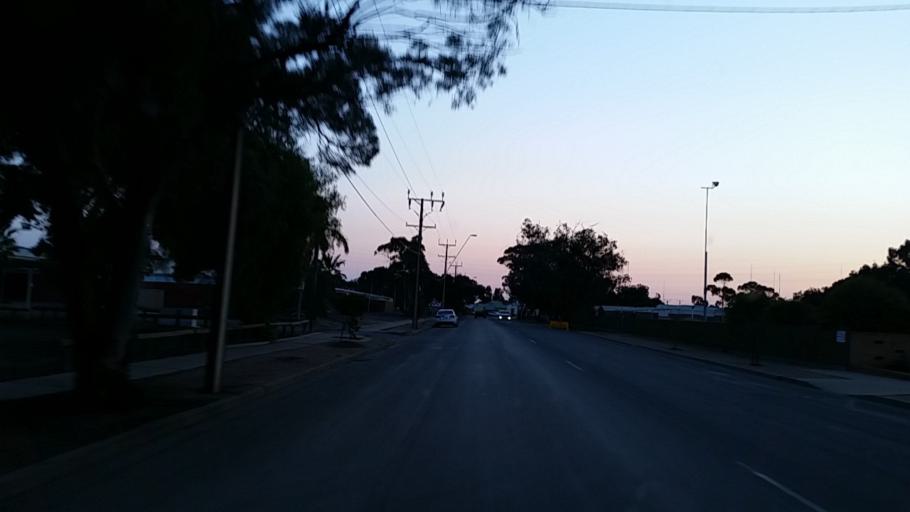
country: AU
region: South Australia
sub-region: Port Pirie City and Dists
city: Port Pirie
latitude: -33.1829
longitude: 138.0062
